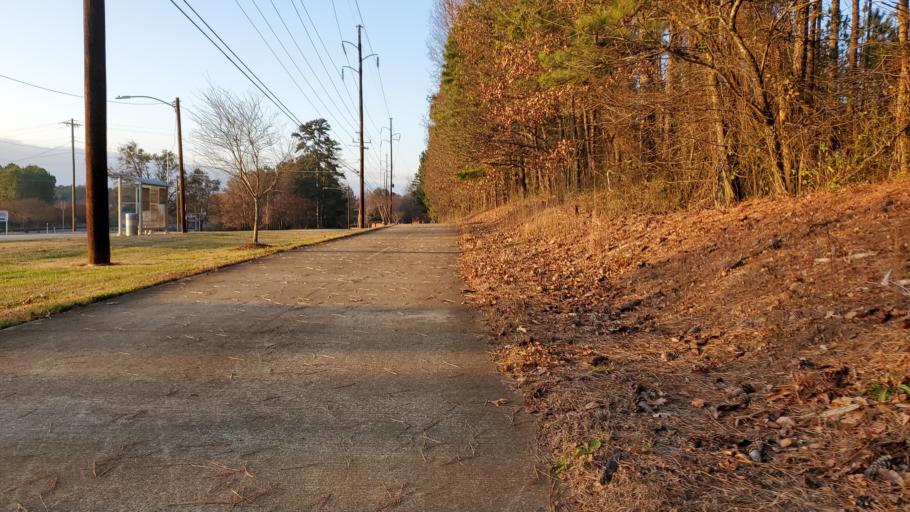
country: US
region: Georgia
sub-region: DeKalb County
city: Stone Mountain
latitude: 33.8204
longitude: -84.1858
